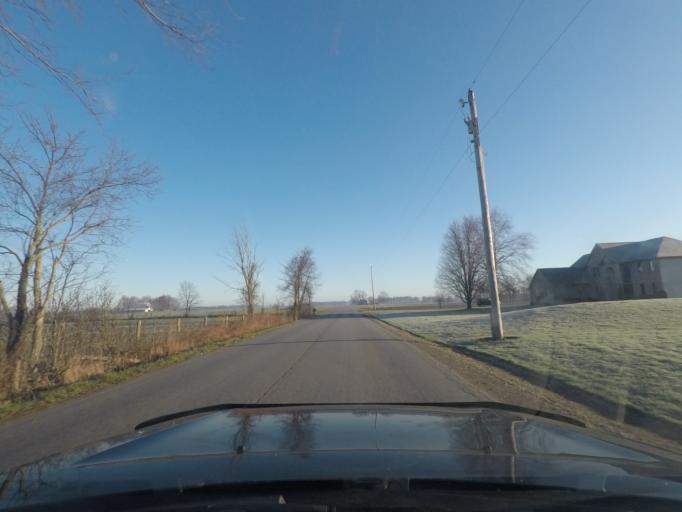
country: US
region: Indiana
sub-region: Elkhart County
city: Dunlap
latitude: 41.5578
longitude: -85.9249
